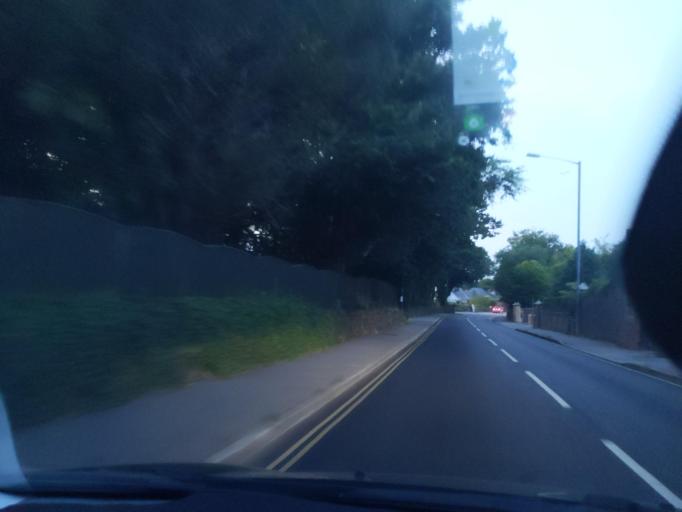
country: GB
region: England
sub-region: Cornwall
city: Camborne
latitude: 50.2083
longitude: -5.3045
